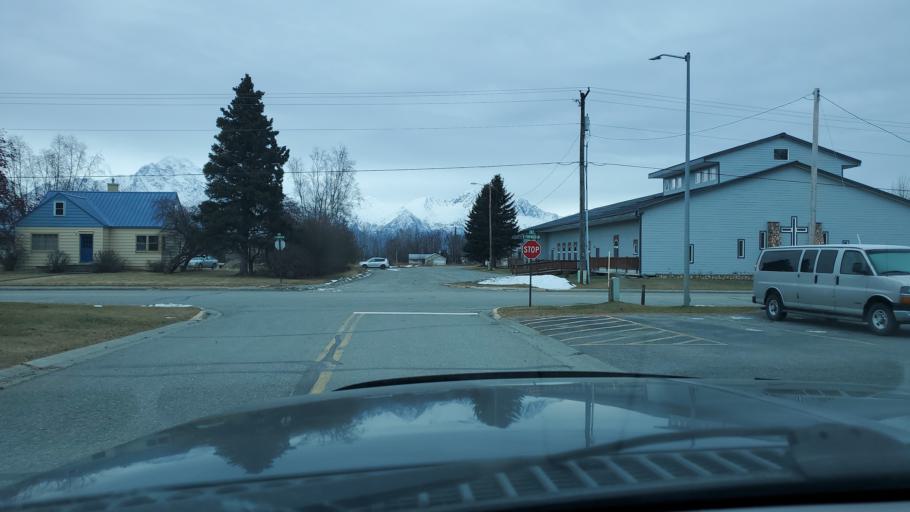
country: US
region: Alaska
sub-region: Matanuska-Susitna Borough
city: Palmer
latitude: 61.5981
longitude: -149.1061
